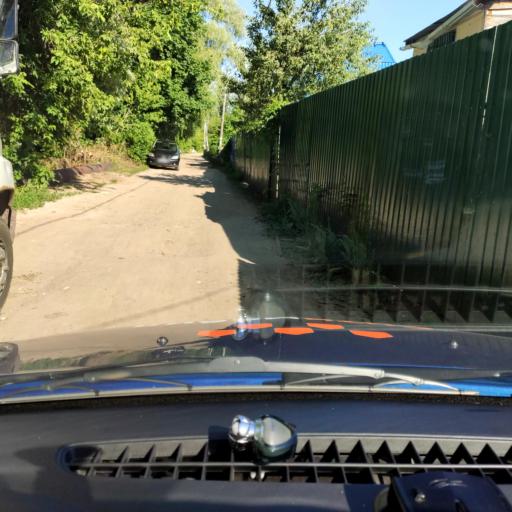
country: RU
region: Voronezj
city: Strelitsa
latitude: 51.6104
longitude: 38.8928
